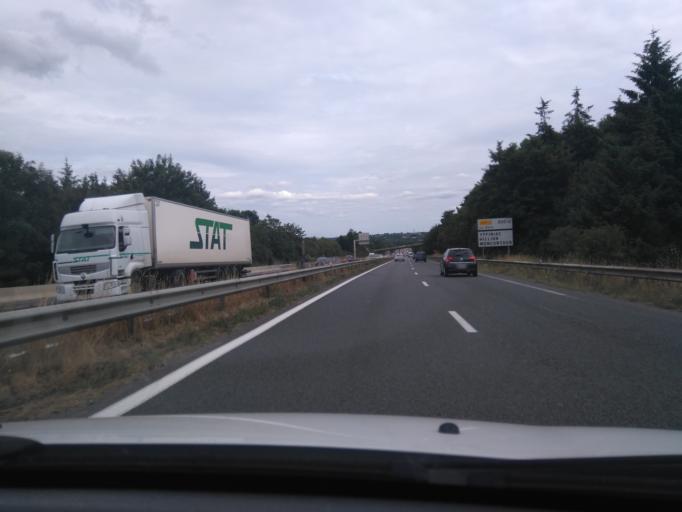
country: FR
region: Brittany
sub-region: Departement des Cotes-d'Armor
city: Yffiniac
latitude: 48.4824
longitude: -2.6881
